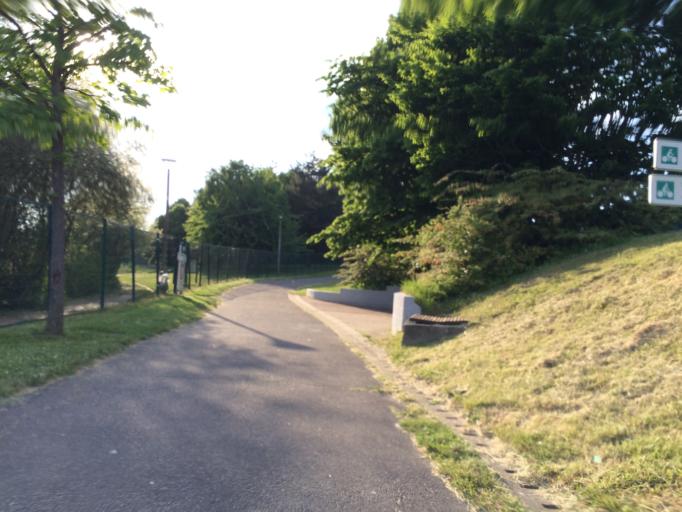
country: FR
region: Ile-de-France
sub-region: Departement de l'Essonne
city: Courcouronnes
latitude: 48.6187
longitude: 2.4190
